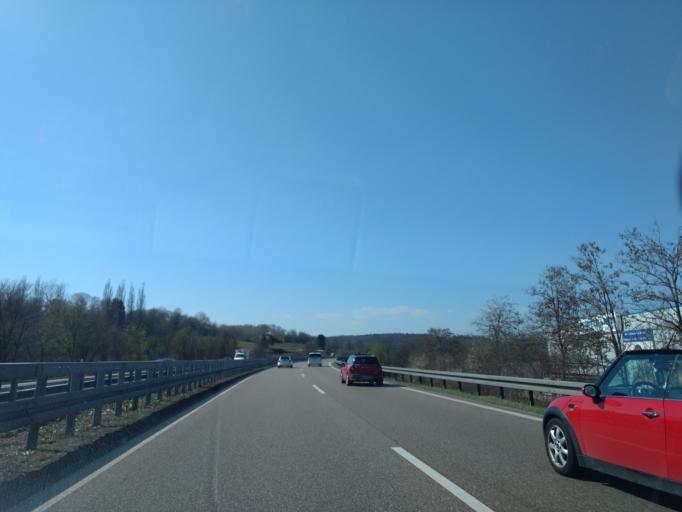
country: DE
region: Baden-Wuerttemberg
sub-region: Regierungsbezirk Stuttgart
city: Plochingen
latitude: 48.7016
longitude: 9.4332
